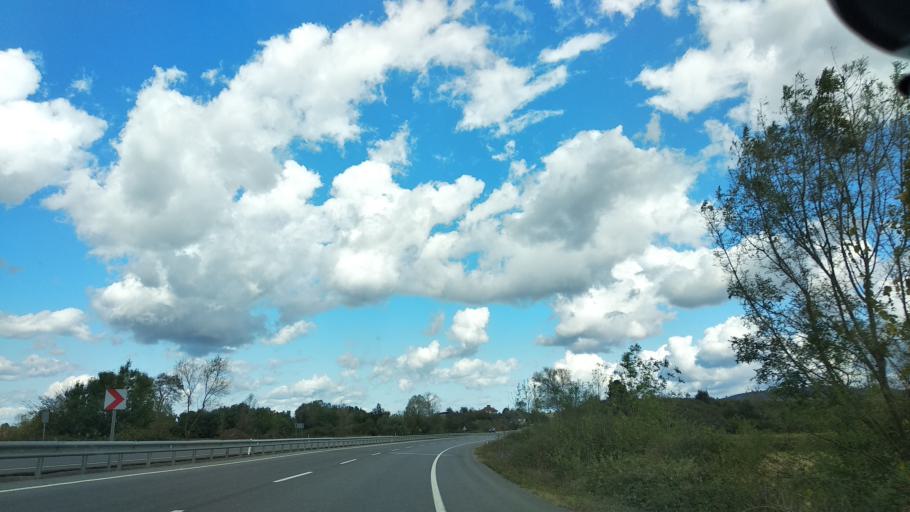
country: TR
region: Sakarya
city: Ortakoy
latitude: 41.0041
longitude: 30.6049
